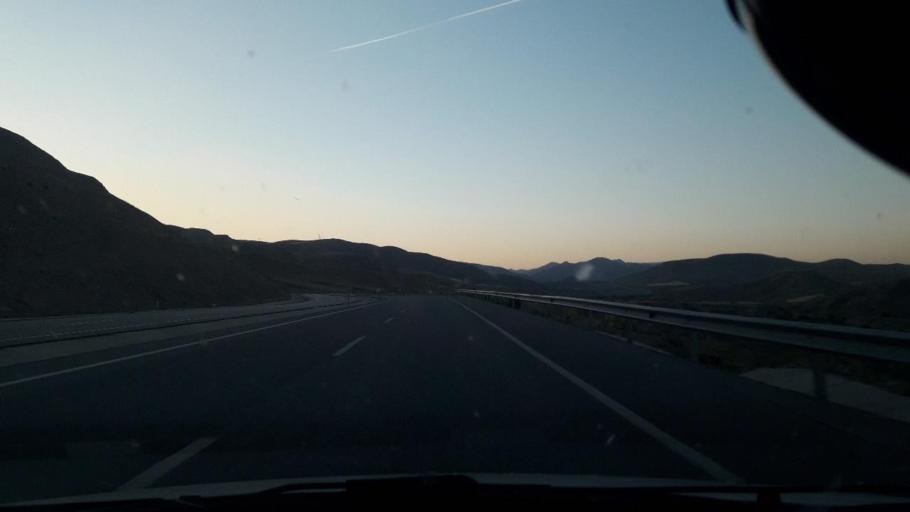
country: TR
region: Malatya
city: Yazihan
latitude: 38.6265
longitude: 38.1637
